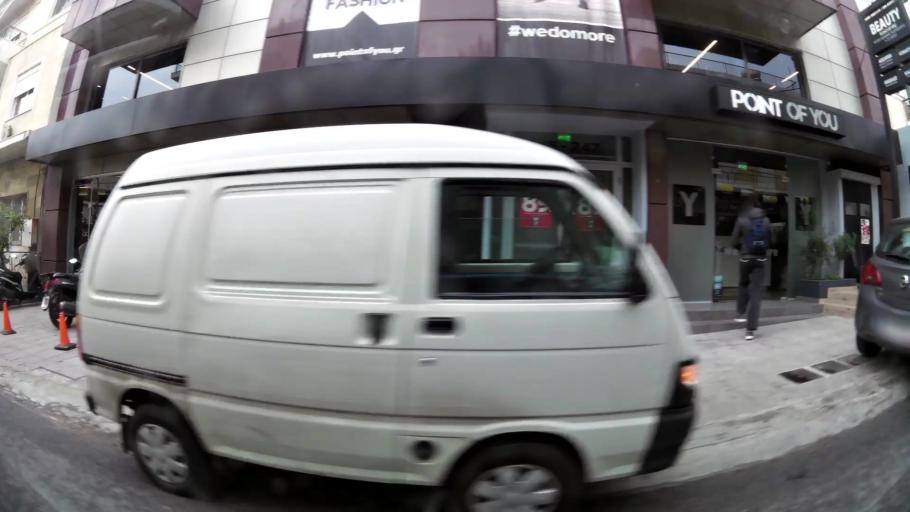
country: GR
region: Attica
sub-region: Nomarchia Athinas
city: Kaisariani
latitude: 37.9563
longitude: 23.7643
